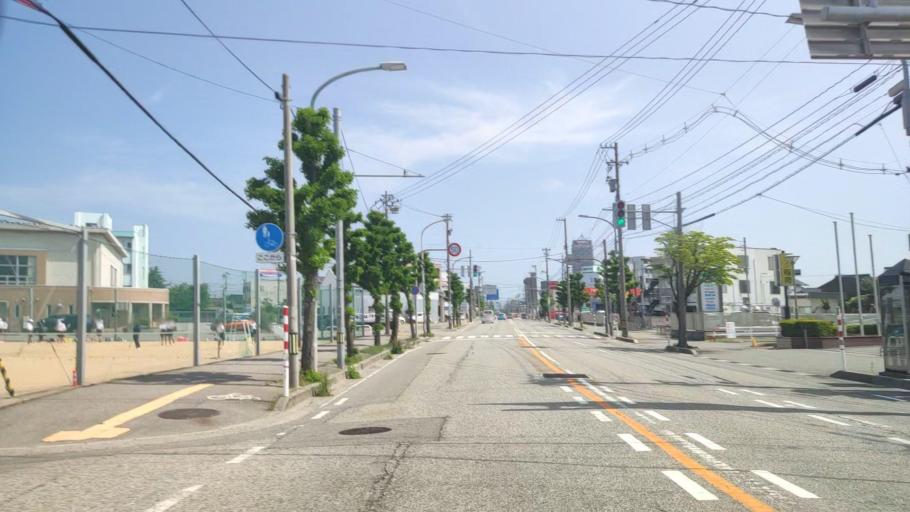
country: JP
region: Toyama
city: Toyama-shi
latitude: 36.7006
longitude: 137.2262
